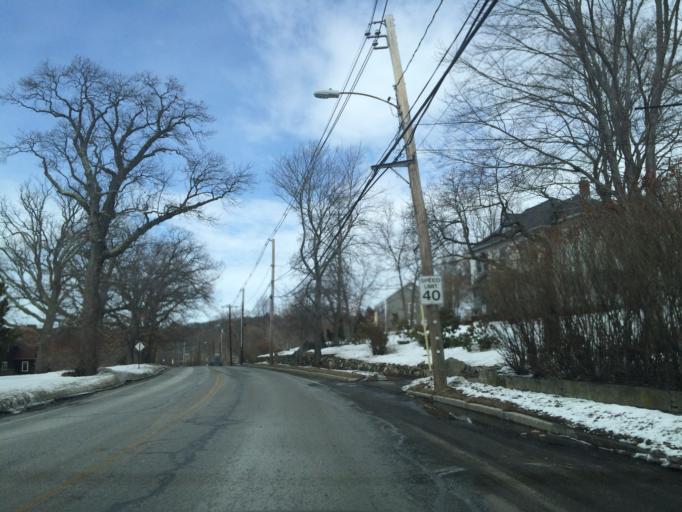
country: US
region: Massachusetts
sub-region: Middlesex County
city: Lexington
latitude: 42.4279
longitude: -71.2309
